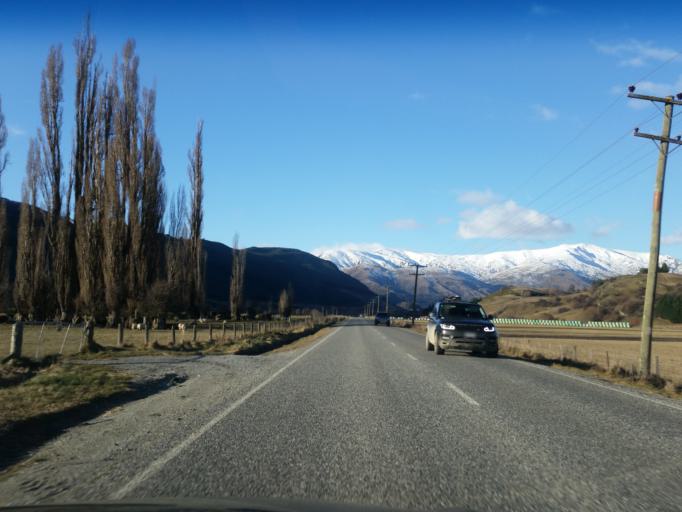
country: NZ
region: Otago
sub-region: Queenstown-Lakes District
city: Arrowtown
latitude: -44.9524
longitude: 168.7488
